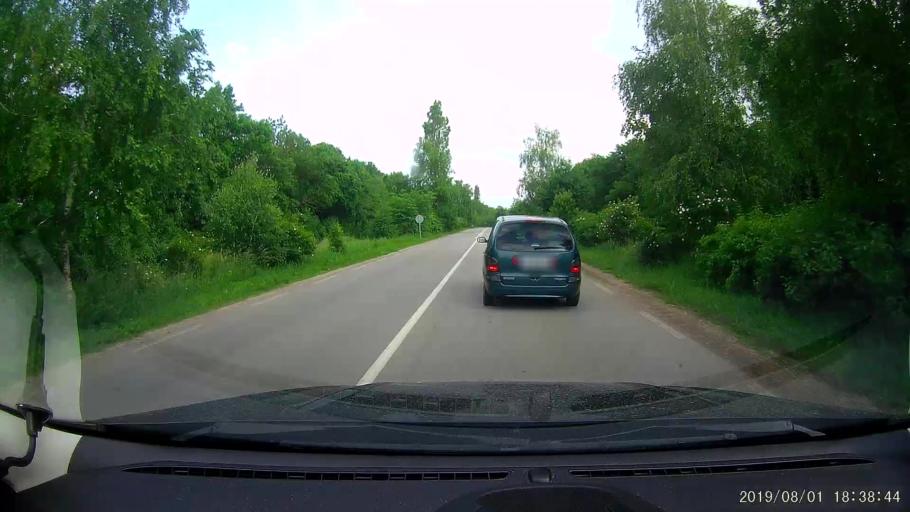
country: BG
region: Shumen
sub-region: Obshtina Khitrino
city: Gara Khitrino
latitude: 43.3982
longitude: 26.9164
